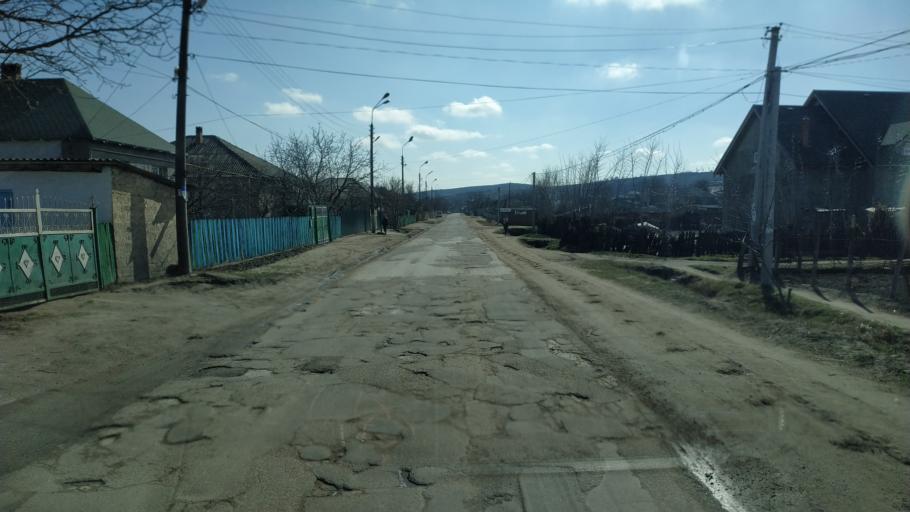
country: MD
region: Hincesti
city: Hincesti
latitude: 46.9593
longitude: 28.6038
